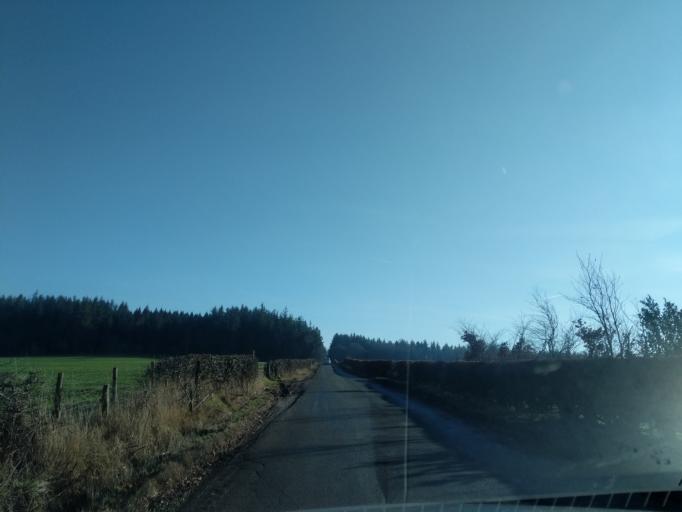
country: GB
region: Scotland
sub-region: South Lanarkshire
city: Carluke
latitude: 55.6948
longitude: -3.8496
